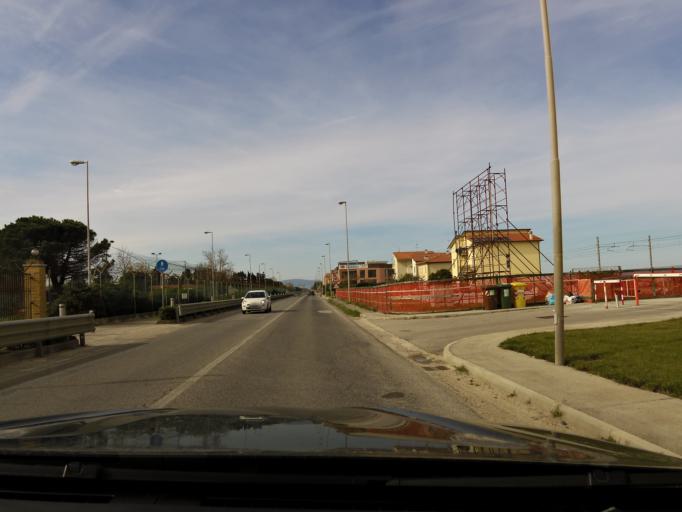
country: IT
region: The Marches
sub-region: Provincia di Macerata
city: Porto Potenza Picena
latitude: 43.3794
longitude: 13.6886
